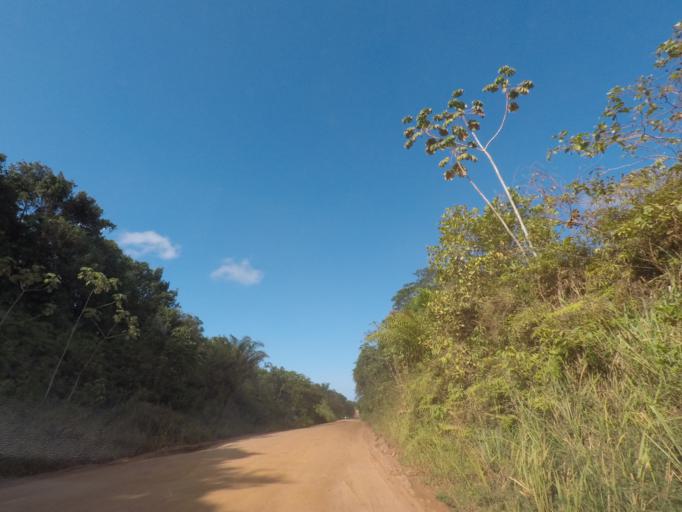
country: BR
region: Bahia
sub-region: Marau
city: Marau
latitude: -14.1269
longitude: -38.9926
